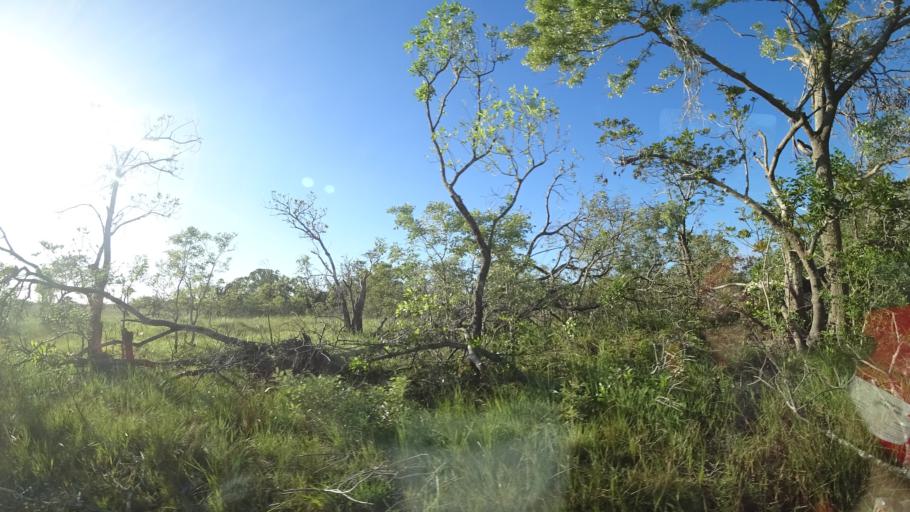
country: MZ
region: Sofala
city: Beira
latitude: -19.5756
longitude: 35.2092
